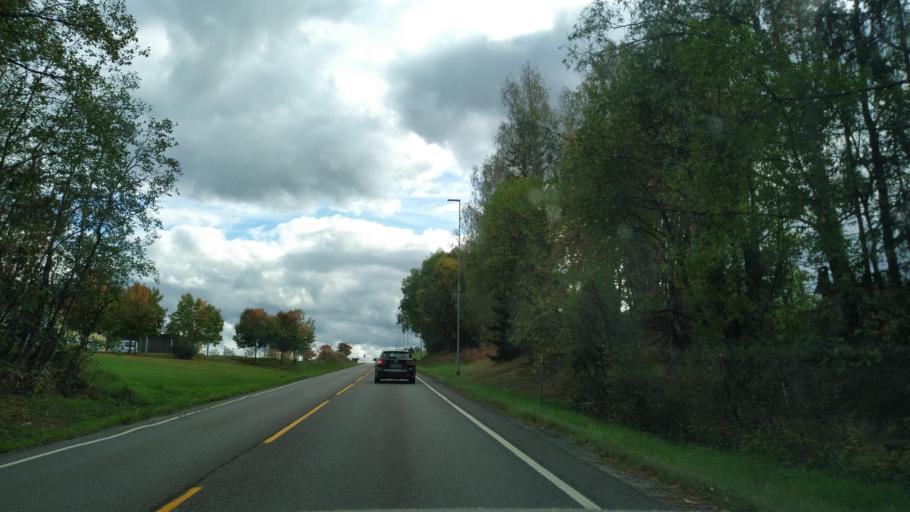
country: NO
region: Akershus
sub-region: Ullensaker
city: Klofta
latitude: 60.0255
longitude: 11.1840
